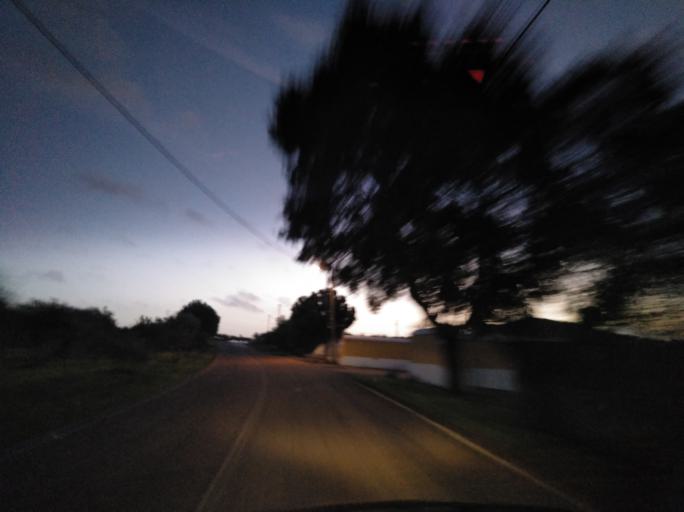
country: PT
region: Portalegre
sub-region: Campo Maior
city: Campo Maior
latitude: 39.0339
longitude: -7.0467
